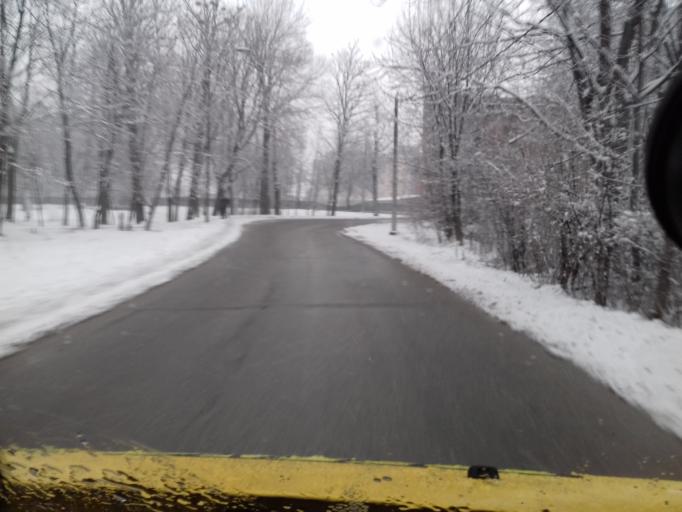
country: BA
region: Federation of Bosnia and Herzegovina
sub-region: Kanton Sarajevo
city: Sarajevo
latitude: 43.8227
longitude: 18.3058
